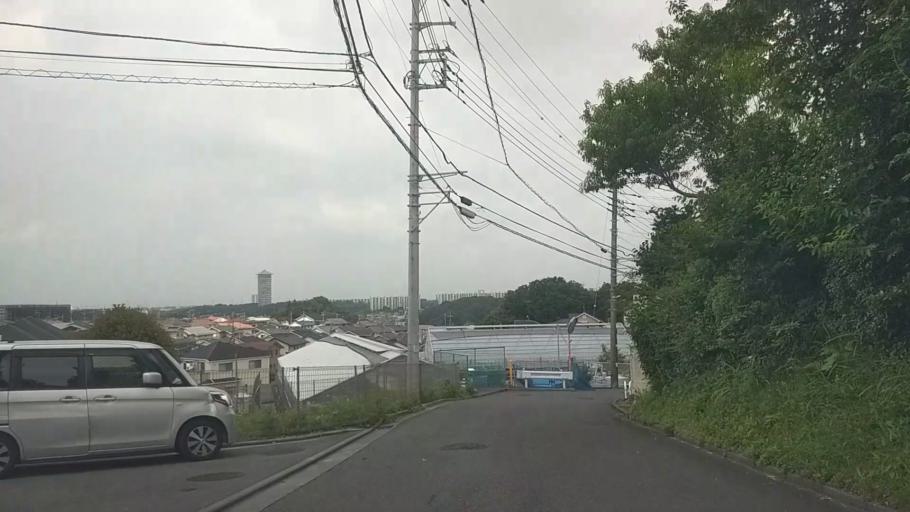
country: JP
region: Kanagawa
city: Fujisawa
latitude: 35.3833
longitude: 139.5103
